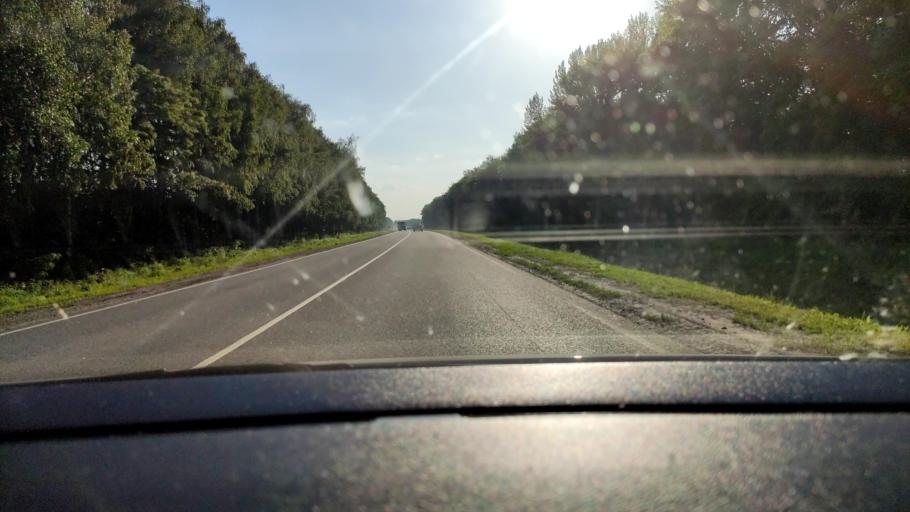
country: RU
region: Voronezj
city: Kashirskoye
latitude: 51.4590
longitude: 39.7937
